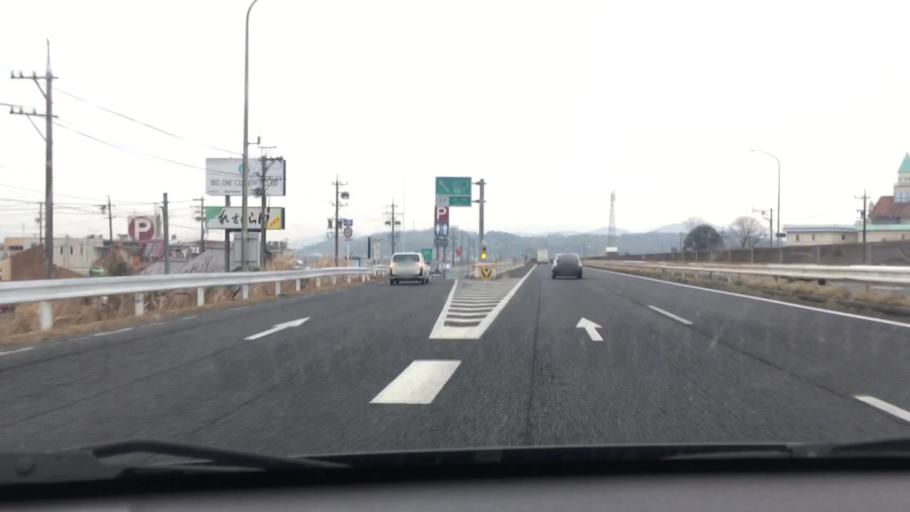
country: JP
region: Mie
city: Ueno-ebisumachi
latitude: 34.7384
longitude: 136.1094
